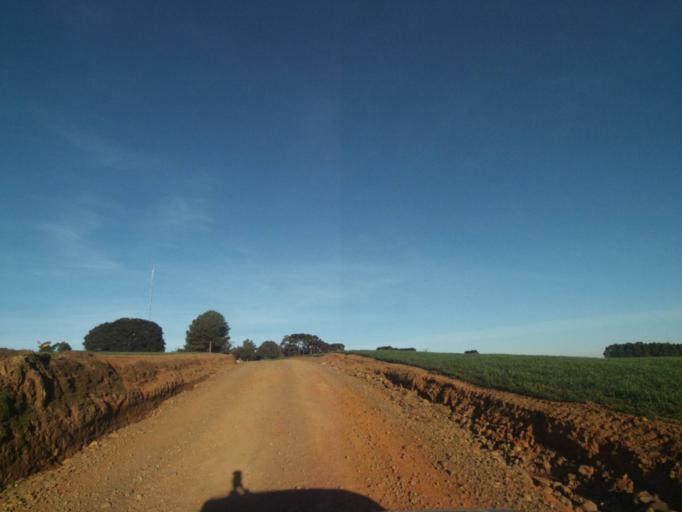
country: BR
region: Parana
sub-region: Telemaco Borba
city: Telemaco Borba
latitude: -24.4712
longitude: -50.5892
